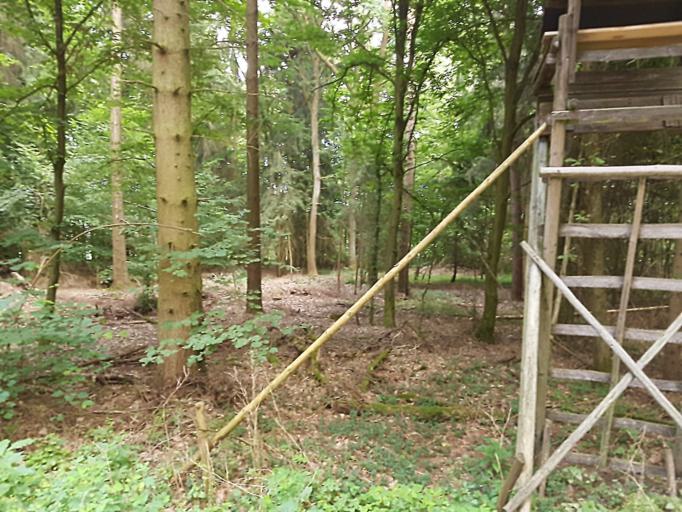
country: DE
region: Bavaria
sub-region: Upper Franconia
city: Litzendorf
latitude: 49.9248
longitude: 10.9910
